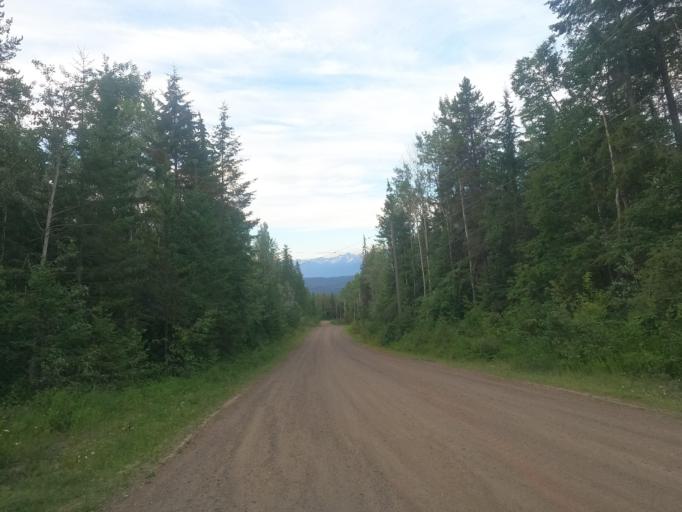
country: CA
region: British Columbia
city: Golden
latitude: 51.4539
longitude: -117.0039
